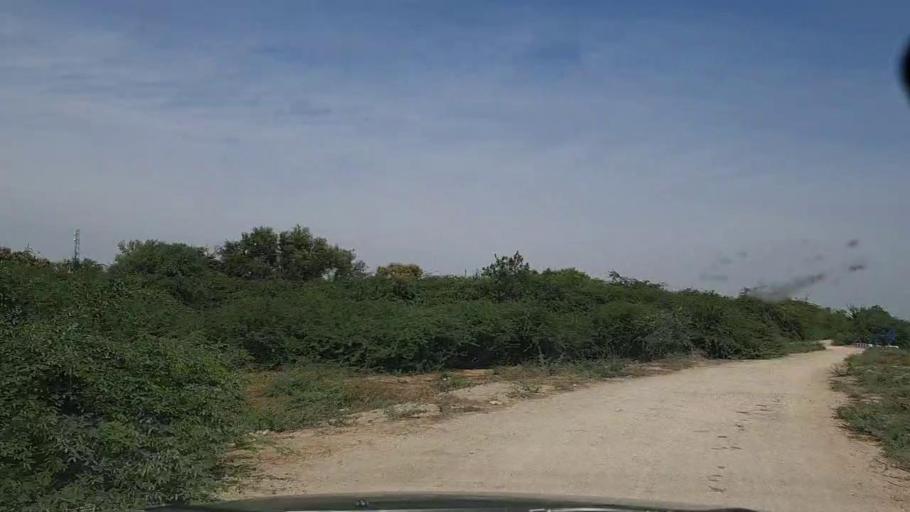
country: PK
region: Sindh
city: Mirpur Batoro
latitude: 24.6538
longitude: 68.1783
